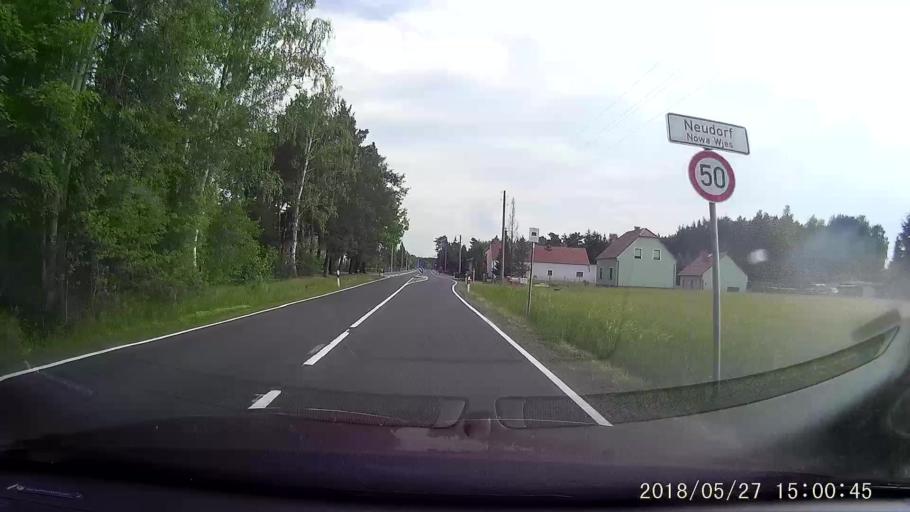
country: DE
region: Saxony
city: Mucka
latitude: 51.3373
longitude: 14.6870
